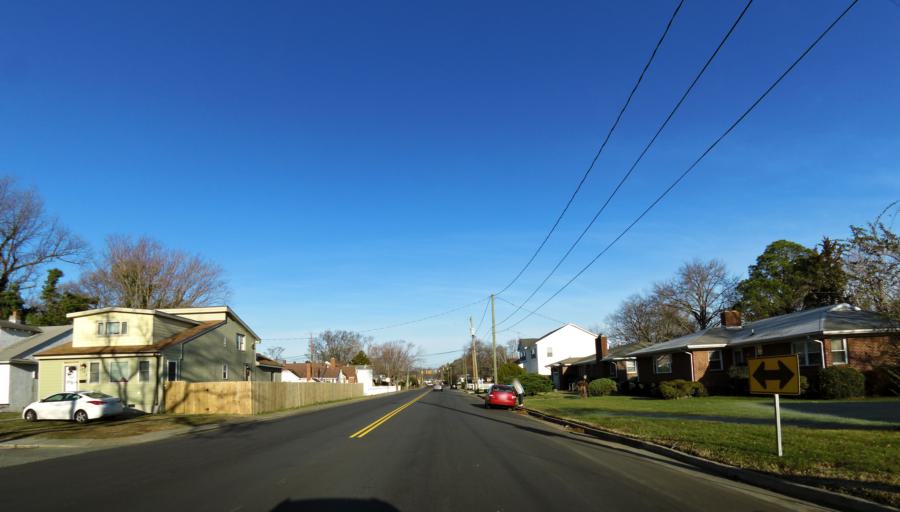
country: US
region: Virginia
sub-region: City of Hampton
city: Hampton
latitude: 37.0073
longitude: -76.3795
